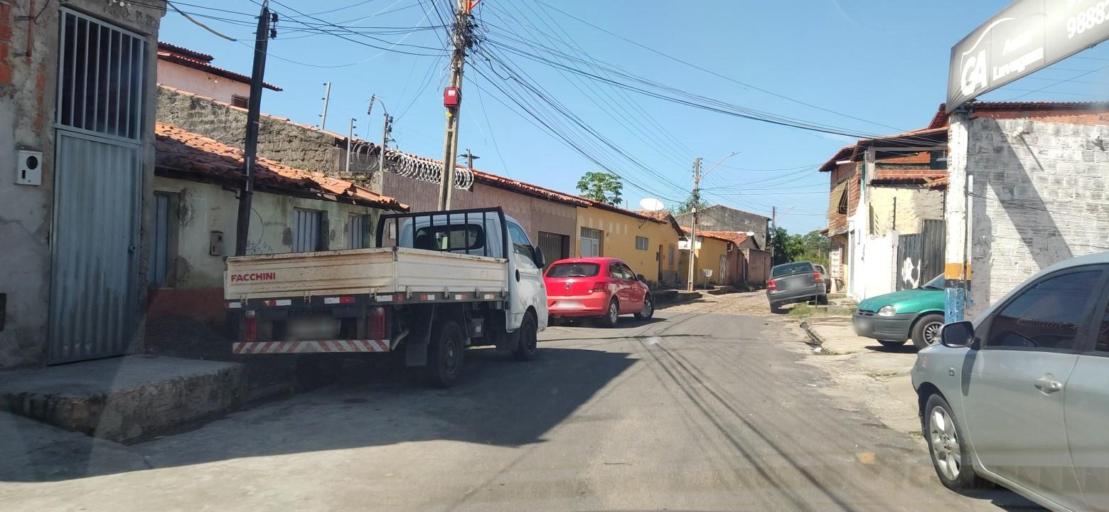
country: BR
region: Piaui
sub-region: Teresina
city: Teresina
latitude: -5.1007
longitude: -42.8012
